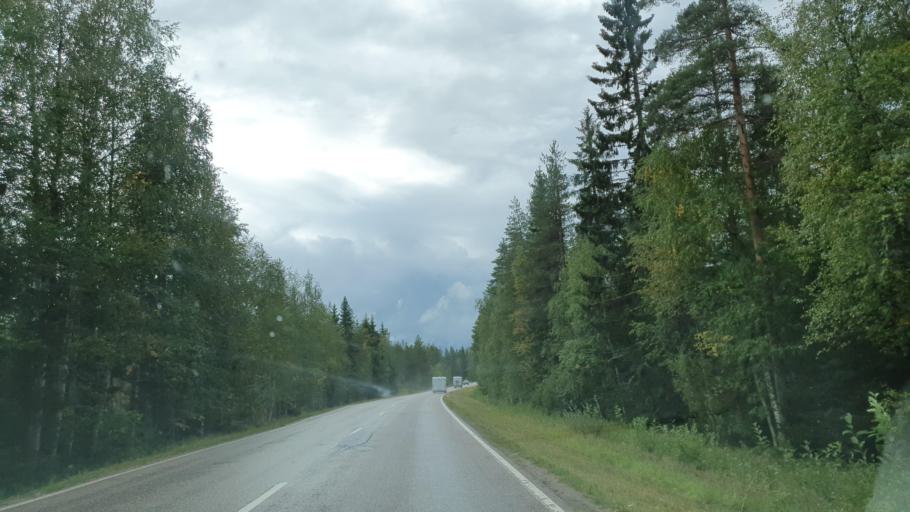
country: FI
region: Kainuu
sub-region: Kehys-Kainuu
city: Puolanka
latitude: 64.9746
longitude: 27.6109
